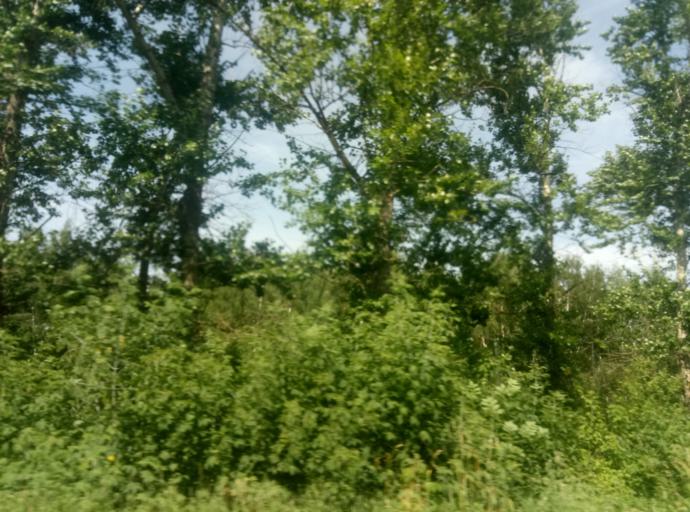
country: RU
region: Tula
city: Kireyevsk
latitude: 53.9283
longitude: 37.9497
